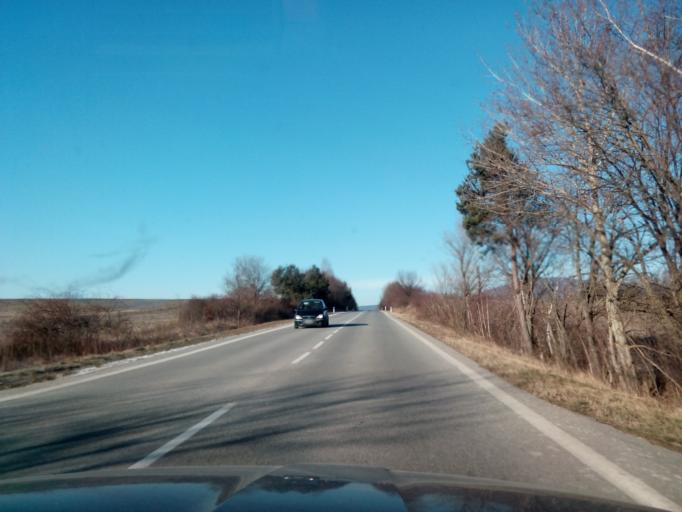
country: SK
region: Kosicky
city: Moldava nad Bodvou
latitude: 48.6878
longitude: 21.0612
